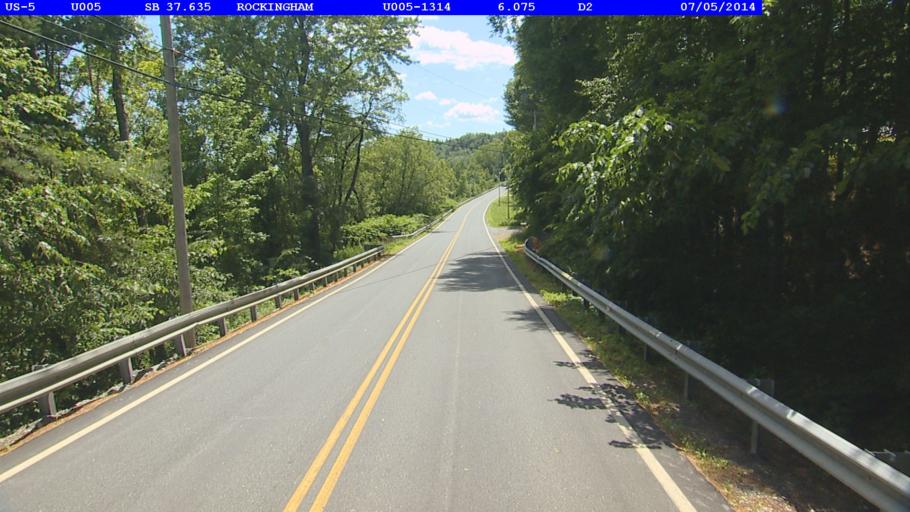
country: US
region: Vermont
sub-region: Windham County
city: Rockingham
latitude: 43.2023
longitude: -72.4507
